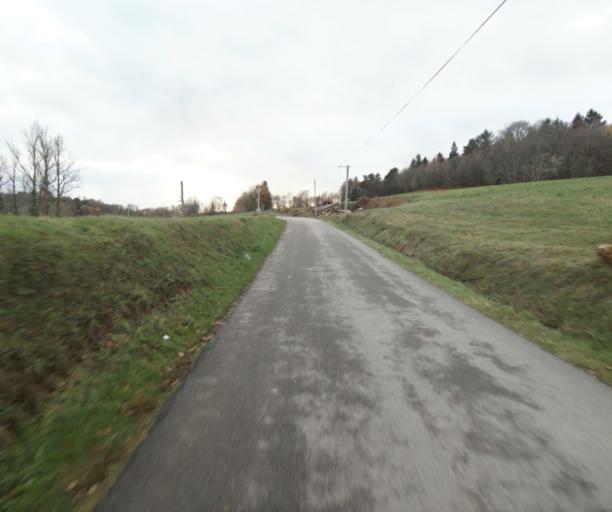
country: FR
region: Limousin
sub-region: Departement de la Correze
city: Sainte-Fortunade
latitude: 45.2252
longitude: 1.7757
